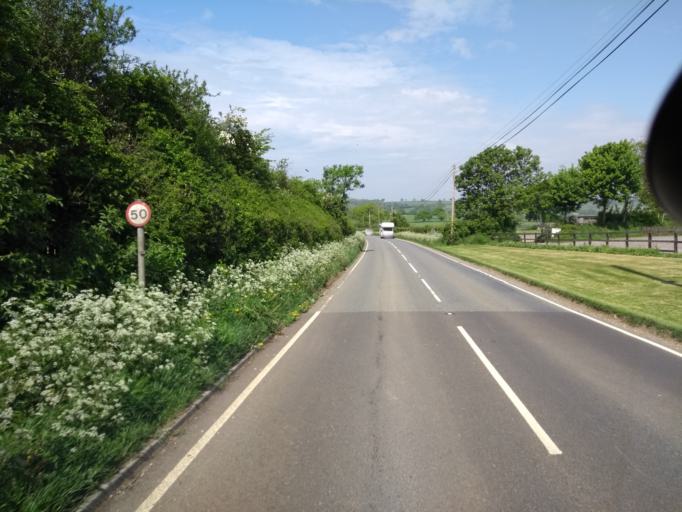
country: GB
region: England
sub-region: Somerset
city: Chard
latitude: 50.8774
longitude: -2.9883
